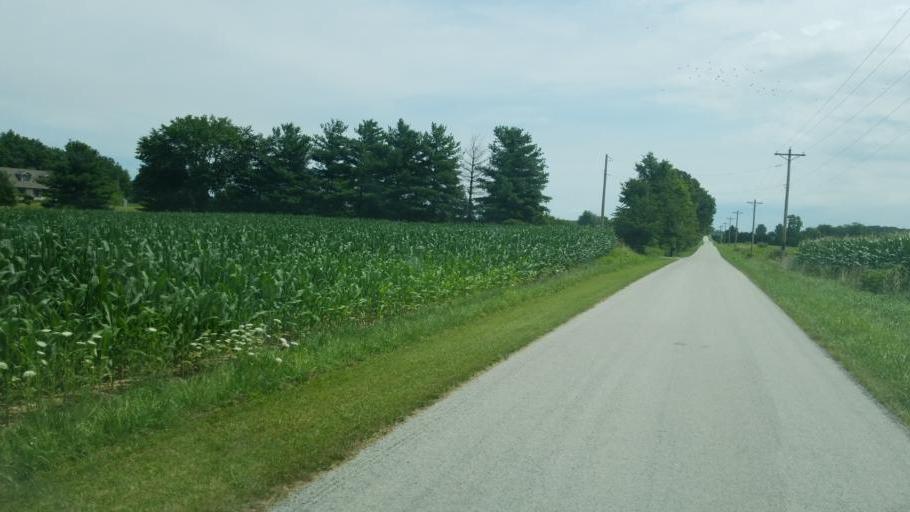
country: US
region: Ohio
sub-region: Crawford County
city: Bucyrus
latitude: 40.8775
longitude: -83.0991
